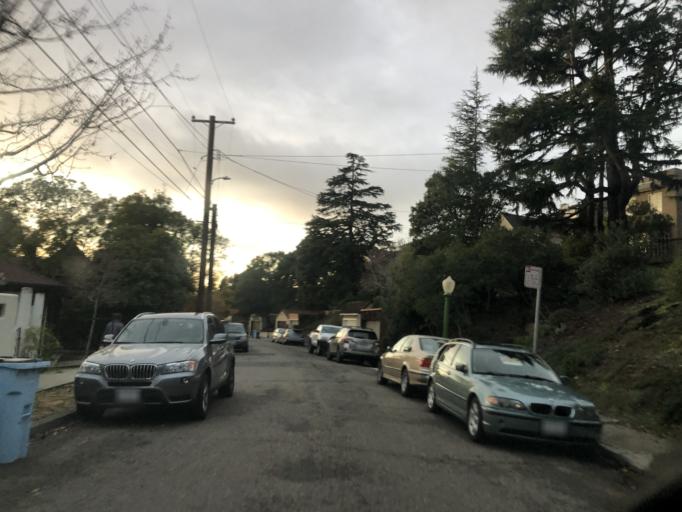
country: US
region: California
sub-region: Alameda County
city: Piedmont
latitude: 37.8526
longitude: -122.2435
